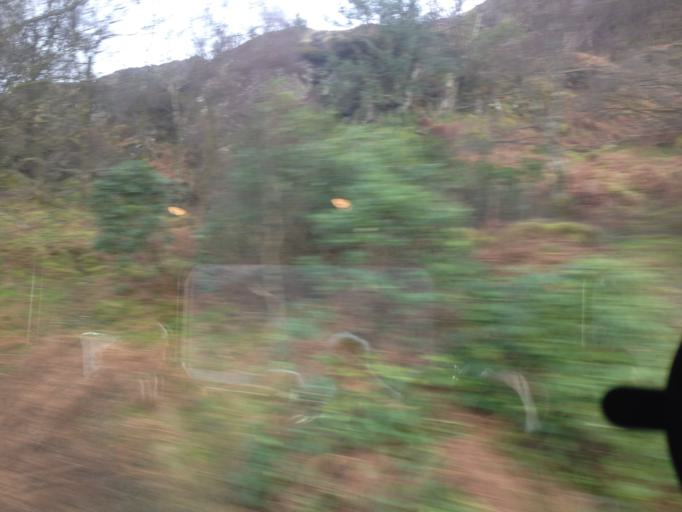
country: GB
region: Scotland
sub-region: Argyll and Bute
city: Garelochhead
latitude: 56.1725
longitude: -4.7775
